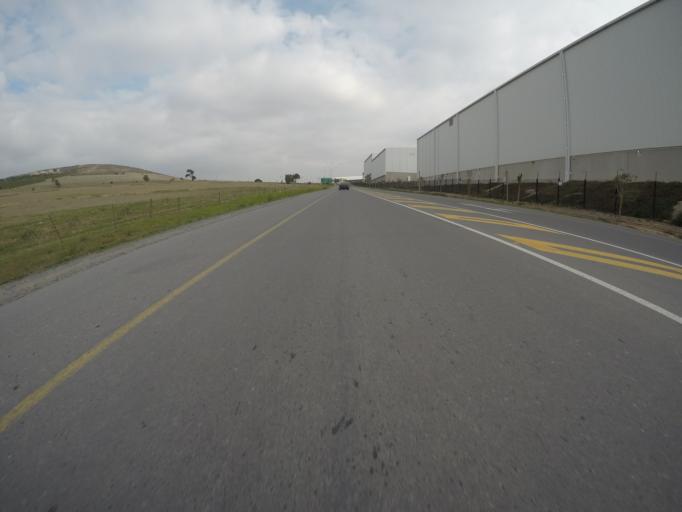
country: ZA
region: Western Cape
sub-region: City of Cape Town
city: Sunset Beach
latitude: -33.8193
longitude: 18.5577
